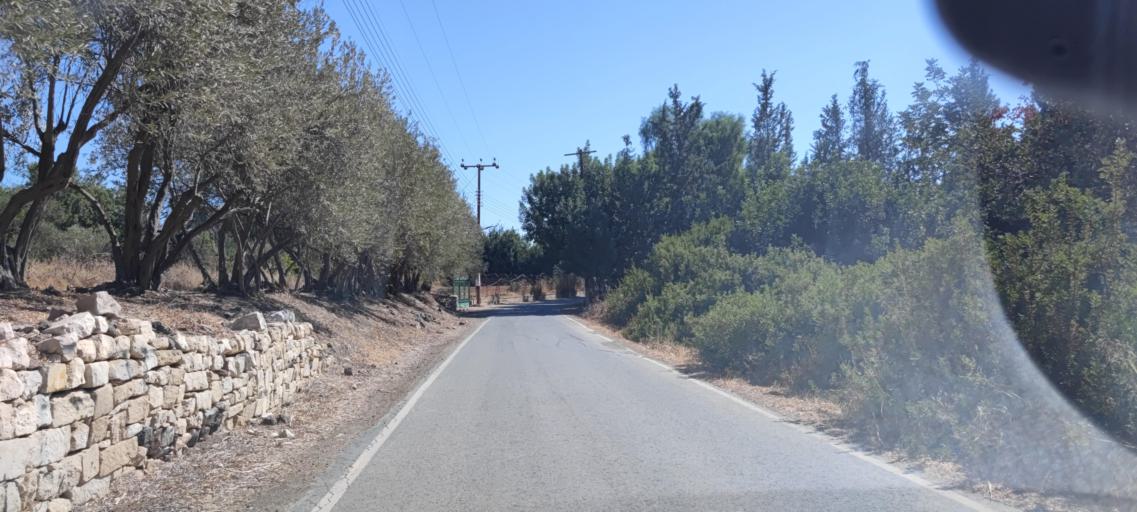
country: CY
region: Limassol
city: Mouttagiaka
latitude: 34.7591
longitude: 33.1067
